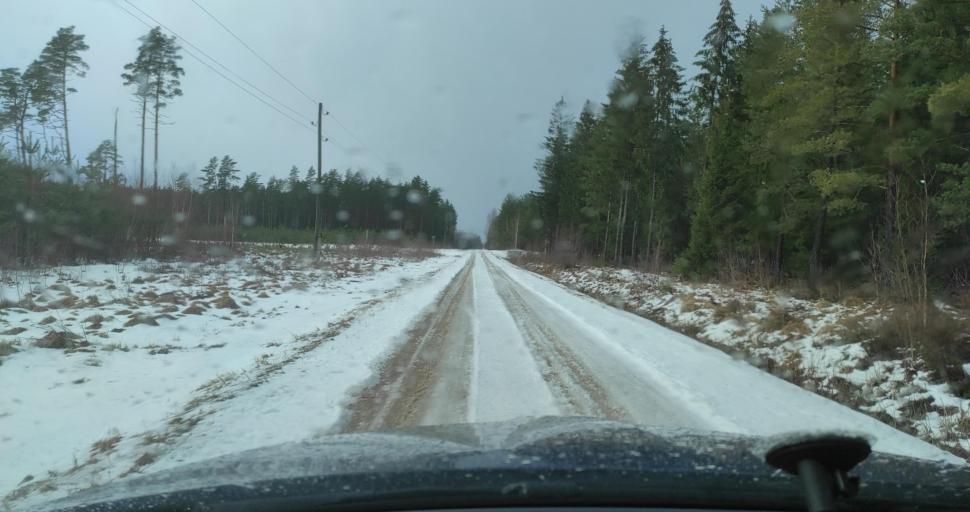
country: LV
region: Dundaga
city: Dundaga
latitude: 57.3837
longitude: 22.1491
